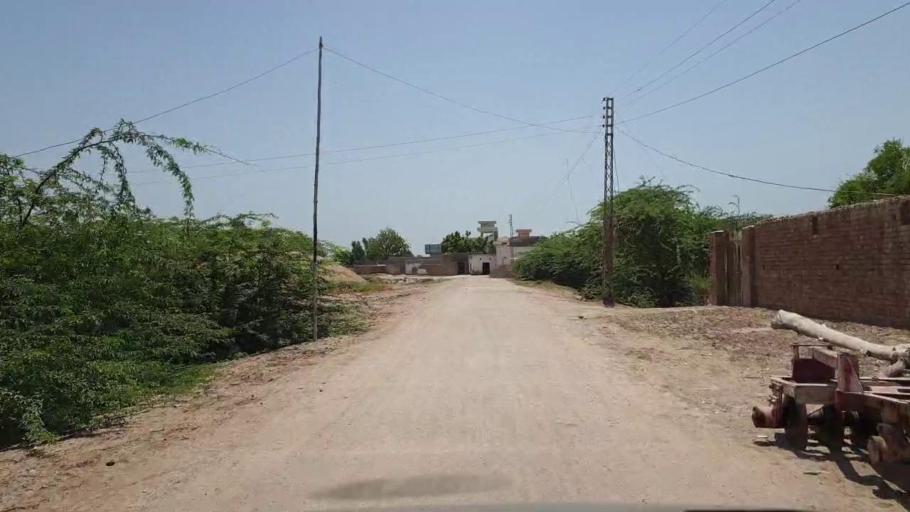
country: PK
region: Sindh
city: Sakrand
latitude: 26.1064
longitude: 68.3918
